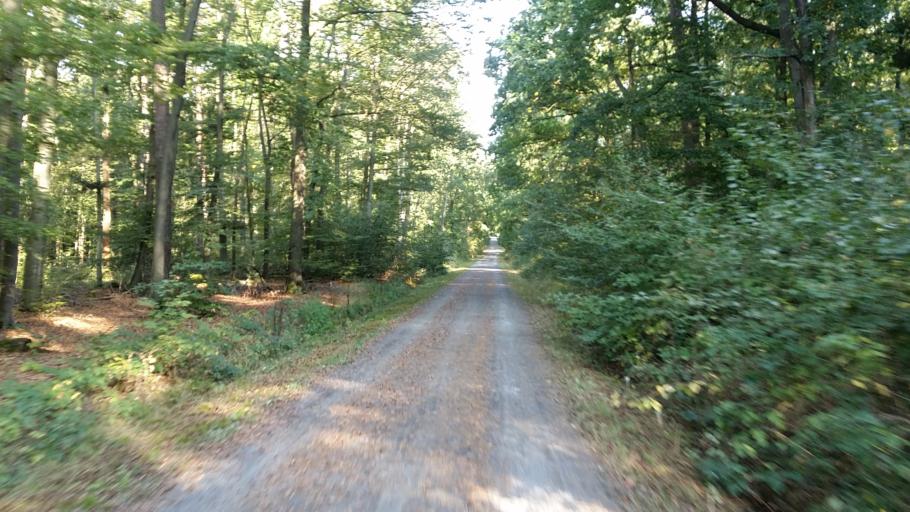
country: DE
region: Hesse
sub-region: Regierungsbezirk Giessen
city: Giessen
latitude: 50.5808
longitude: 8.7178
